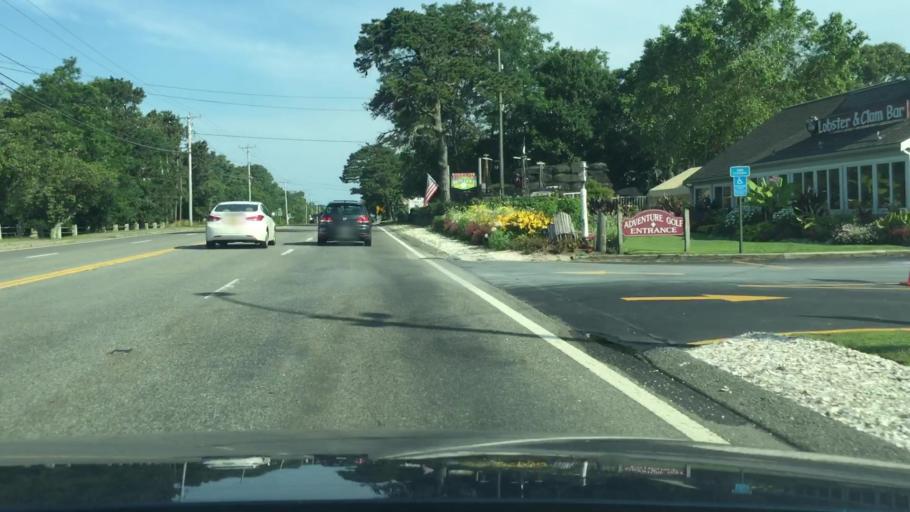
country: US
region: Massachusetts
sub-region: Barnstable County
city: Eastham
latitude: 41.8434
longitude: -69.9829
